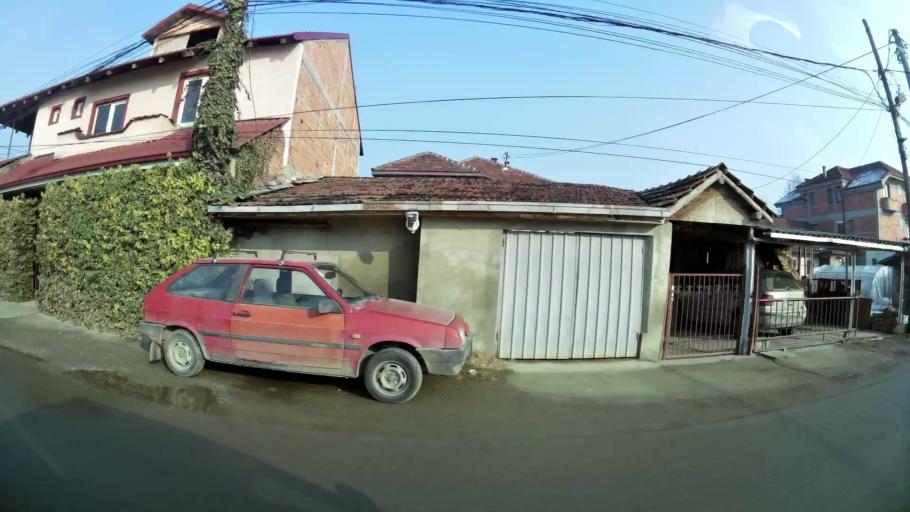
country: MK
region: Ilinden
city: Marino
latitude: 41.9809
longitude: 21.5926
